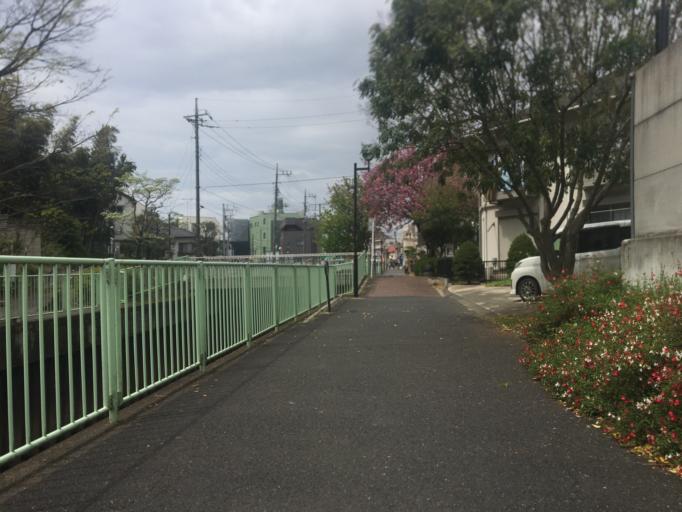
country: JP
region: Tokyo
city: Mitaka-shi
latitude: 35.6867
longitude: 139.6011
